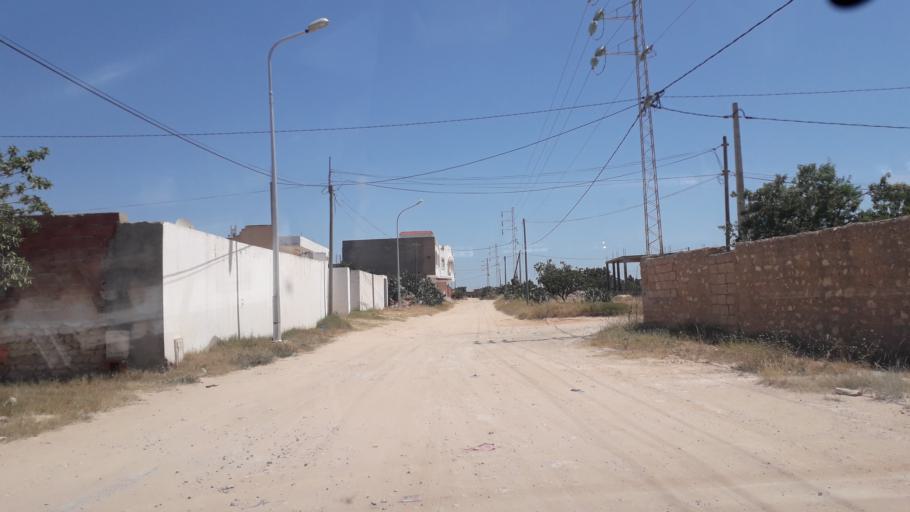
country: TN
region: Safaqis
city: Al Qarmadah
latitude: 34.8289
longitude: 10.7748
